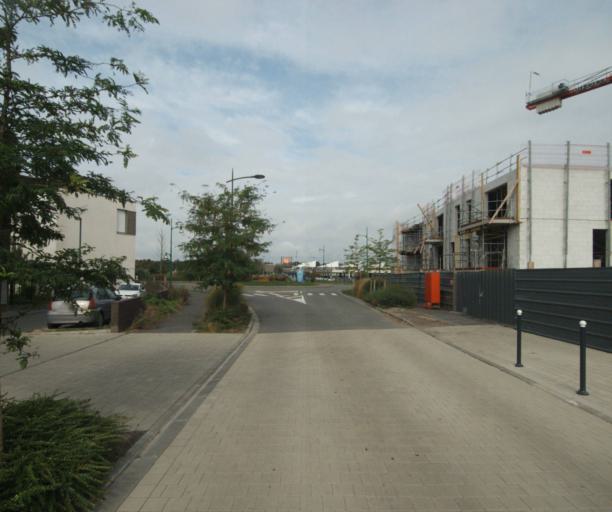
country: FR
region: Nord-Pas-de-Calais
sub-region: Departement du Nord
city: Ronchin
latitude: 50.5852
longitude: 3.0989
